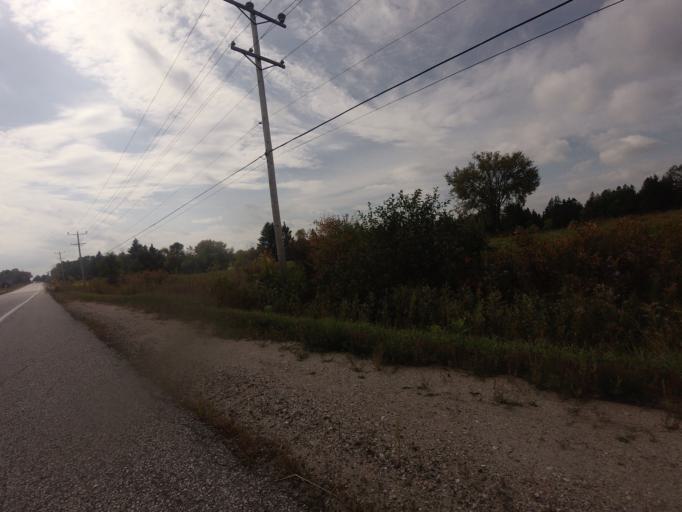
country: CA
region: Quebec
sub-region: Outaouais
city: Wakefield
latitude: 45.8751
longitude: -76.0254
